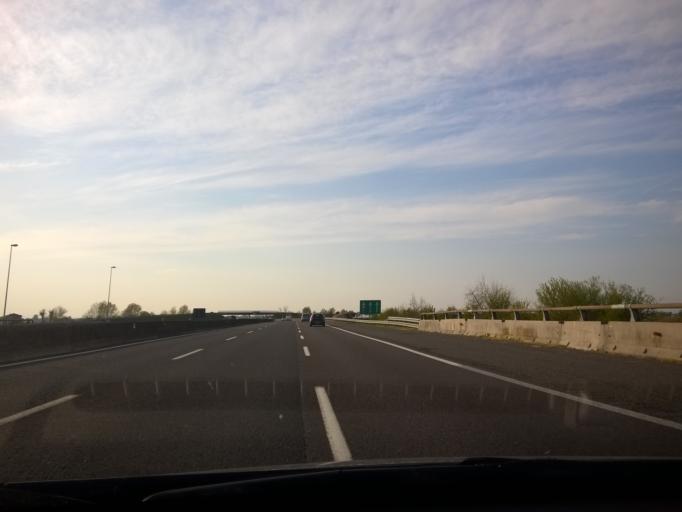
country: IT
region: Emilia-Romagna
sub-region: Forli-Cesena
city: Santa Maria Nuova
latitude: 44.2201
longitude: 12.1725
